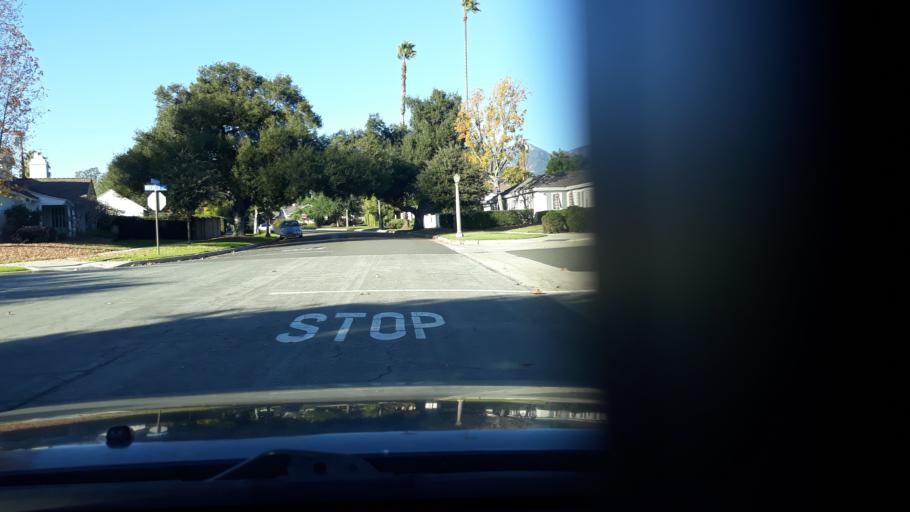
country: US
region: California
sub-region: Los Angeles County
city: San Marino
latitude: 34.1197
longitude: -118.1036
